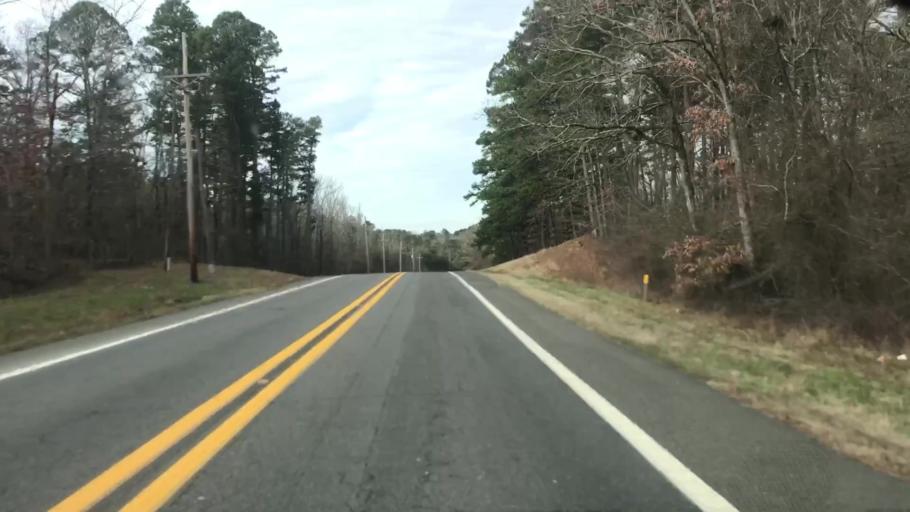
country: US
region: Arkansas
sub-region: Montgomery County
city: Mount Ida
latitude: 34.6086
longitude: -93.6784
